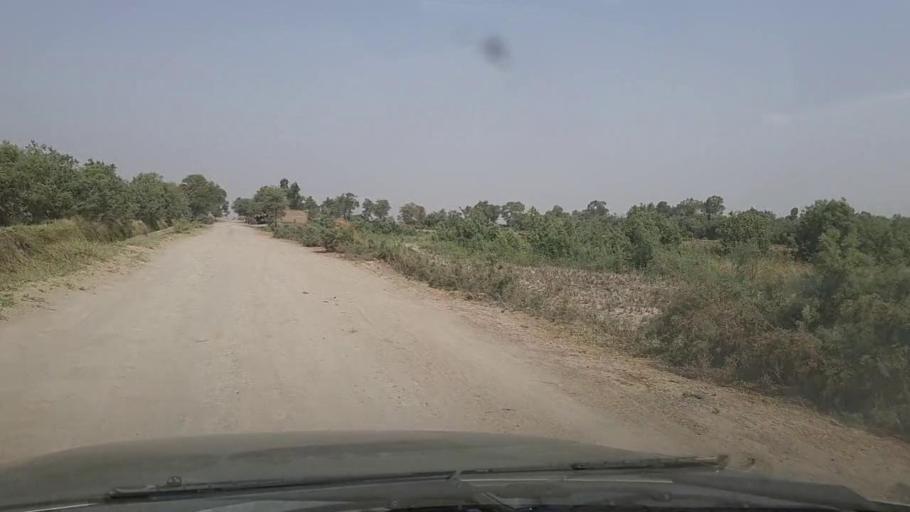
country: PK
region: Sindh
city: Thul
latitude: 28.4010
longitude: 68.7077
